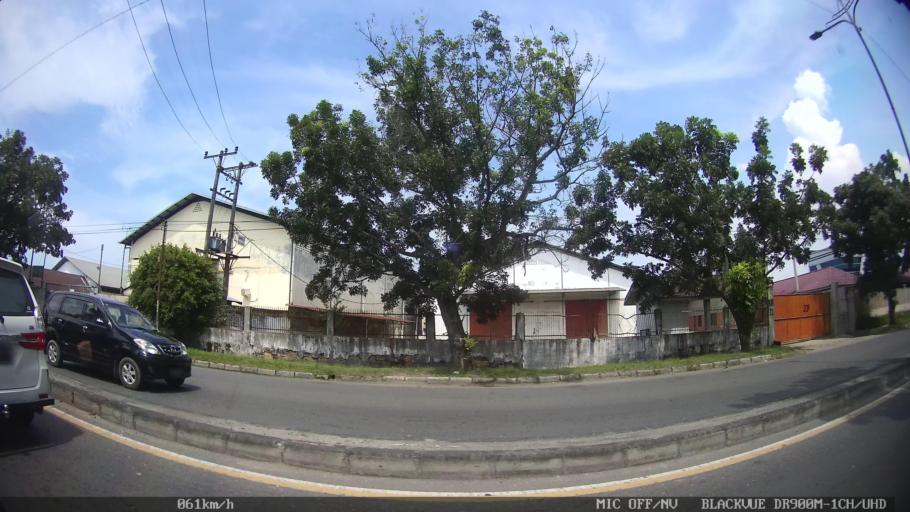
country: ID
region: North Sumatra
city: Labuhan Deli
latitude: 3.6732
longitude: 98.6663
